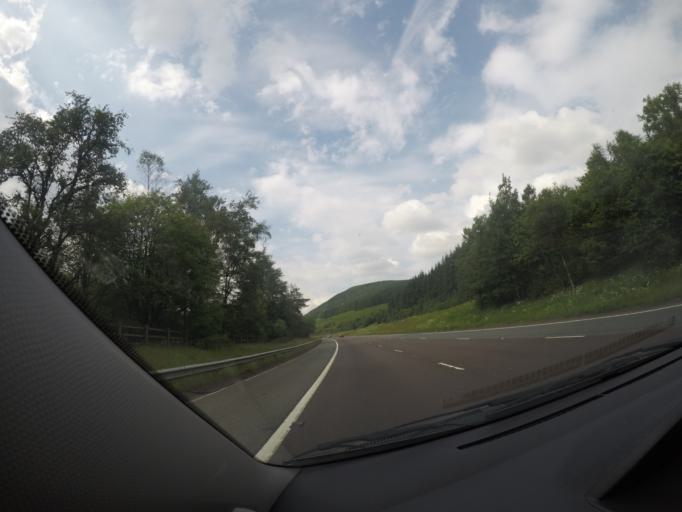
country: GB
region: Scotland
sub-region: Dumfries and Galloway
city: Moffat
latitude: 55.3714
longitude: -3.5129
